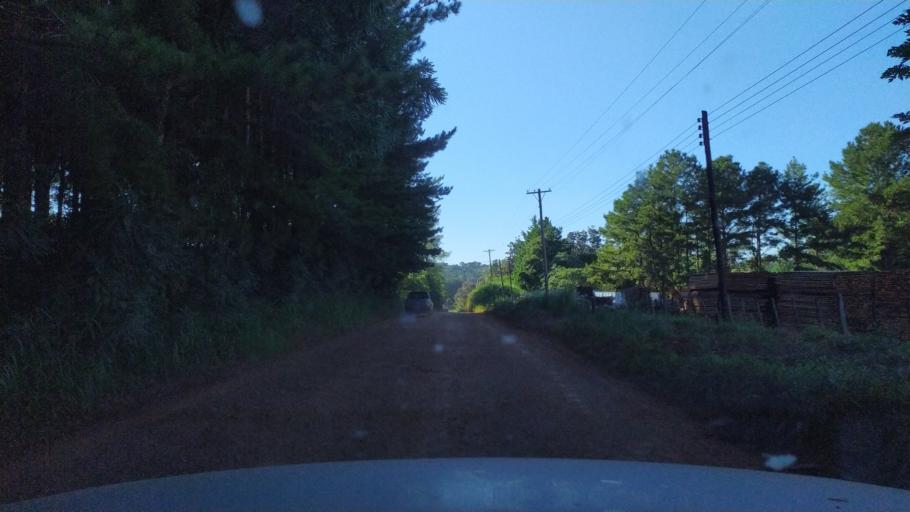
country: AR
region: Misiones
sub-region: Departamento de Montecarlo
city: Montecarlo
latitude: -26.6275
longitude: -54.6915
